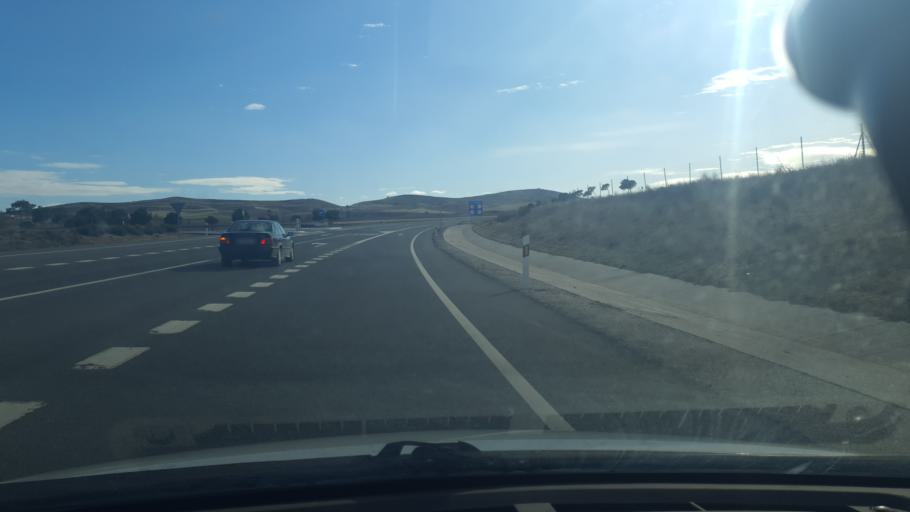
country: ES
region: Castille and Leon
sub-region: Provincia de Avila
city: Penalba de Avila
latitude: 40.7828
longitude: -4.7563
